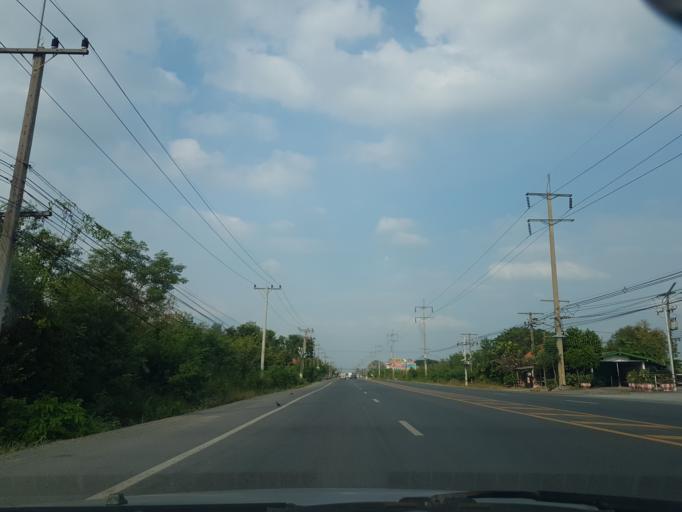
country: TH
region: Phra Nakhon Si Ayutthaya
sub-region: Amphoe Tha Ruea
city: Tha Ruea
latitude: 14.5783
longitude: 100.7284
